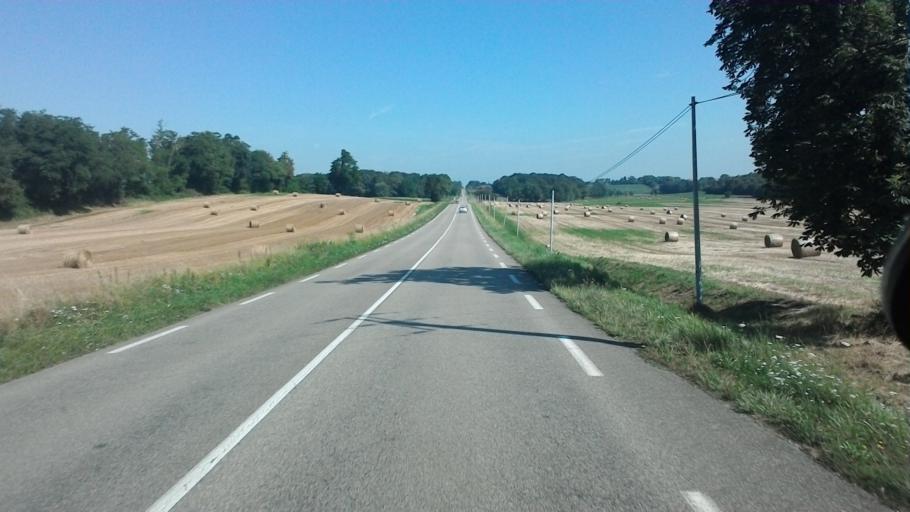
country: FR
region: Rhone-Alpes
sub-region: Departement de l'Ain
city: Saint-Trivier-de-Courtes
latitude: 46.4716
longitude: 5.0756
